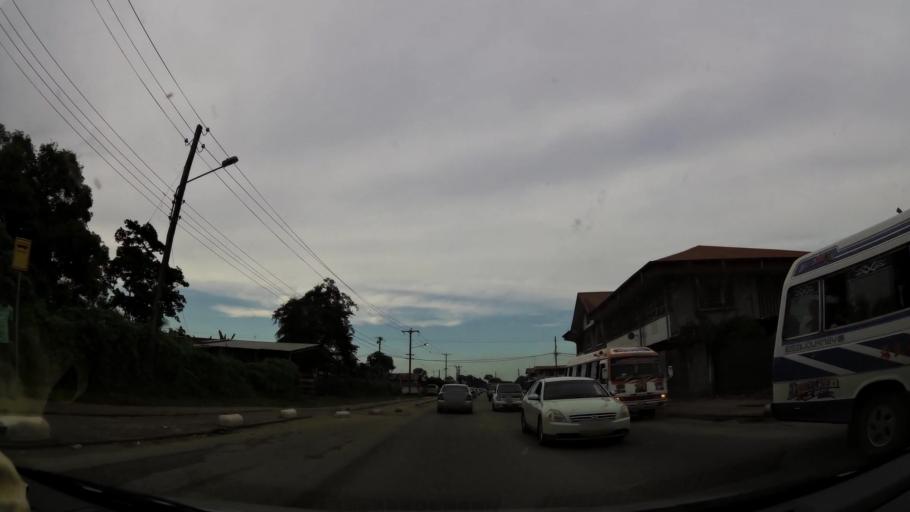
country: SR
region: Paramaribo
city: Paramaribo
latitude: 5.7975
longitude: -55.1895
